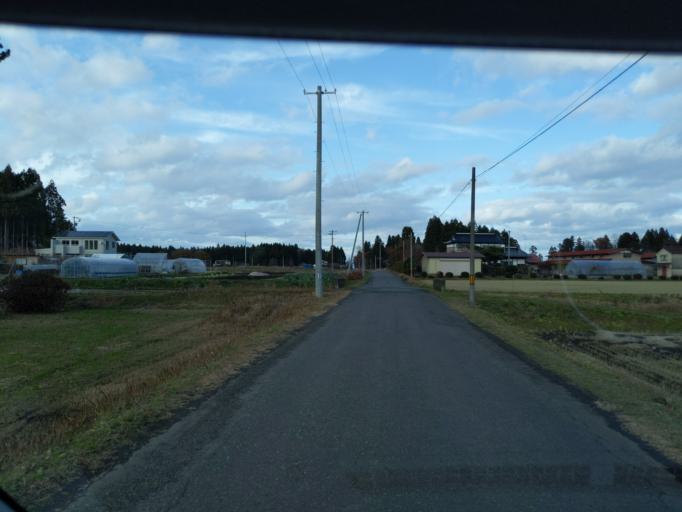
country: JP
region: Iwate
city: Mizusawa
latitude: 39.1122
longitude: 141.0922
